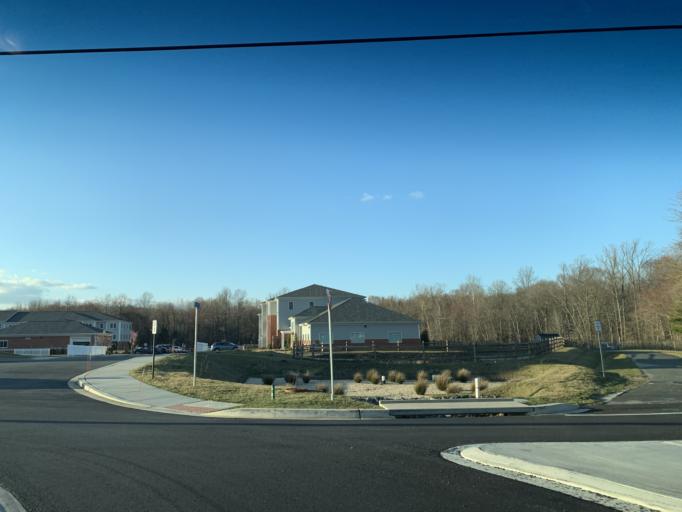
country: US
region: Maryland
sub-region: Harford County
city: Aberdeen
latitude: 39.5272
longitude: -76.1776
